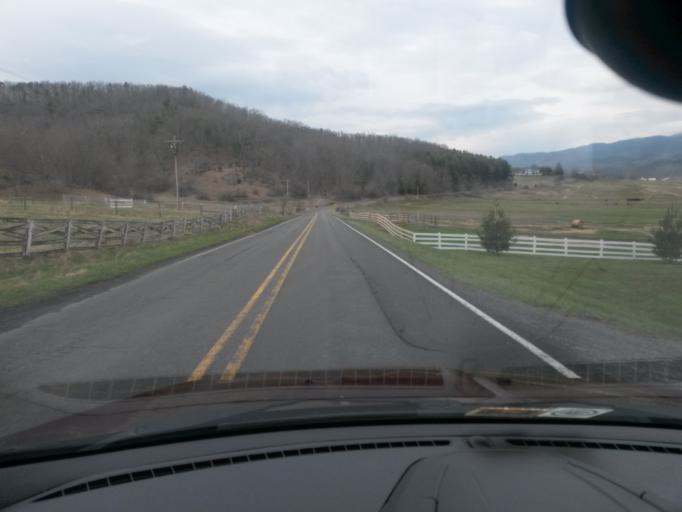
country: US
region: Virginia
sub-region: Bath County
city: Warm Springs
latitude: 38.2087
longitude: -79.7228
